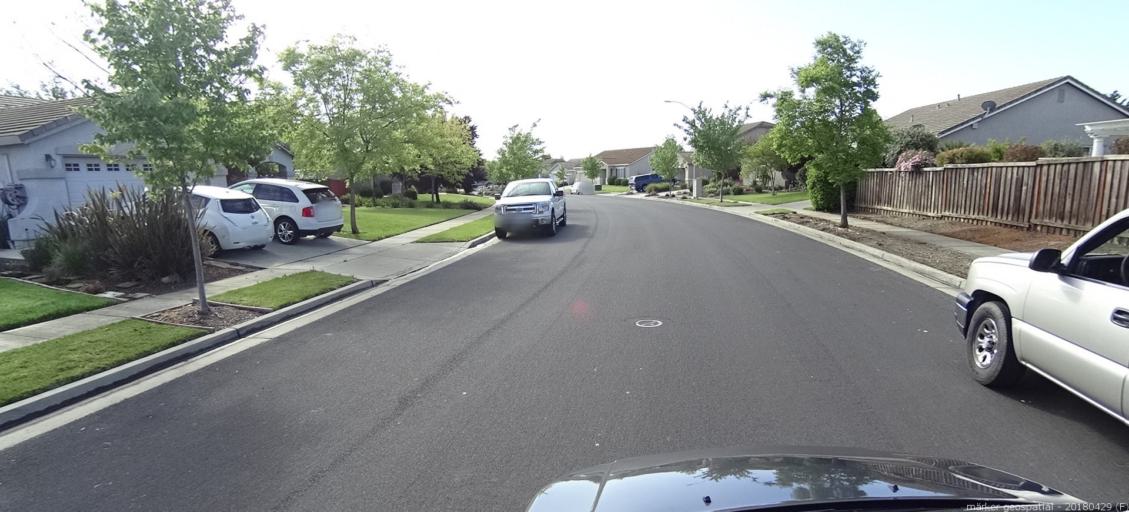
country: US
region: California
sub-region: Yolo County
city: West Sacramento
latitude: 38.5376
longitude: -121.5638
